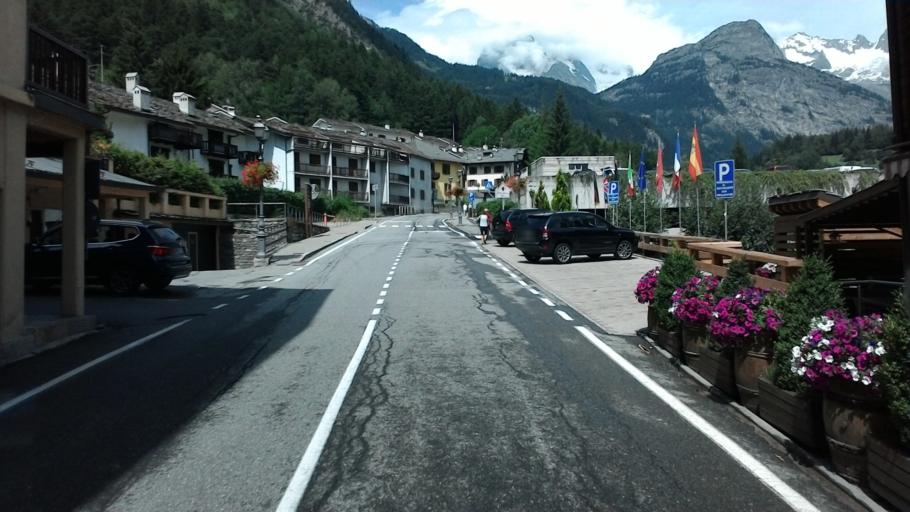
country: IT
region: Aosta Valley
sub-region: Valle d'Aosta
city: Pre Saint Didier
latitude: 45.7641
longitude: 6.9858
